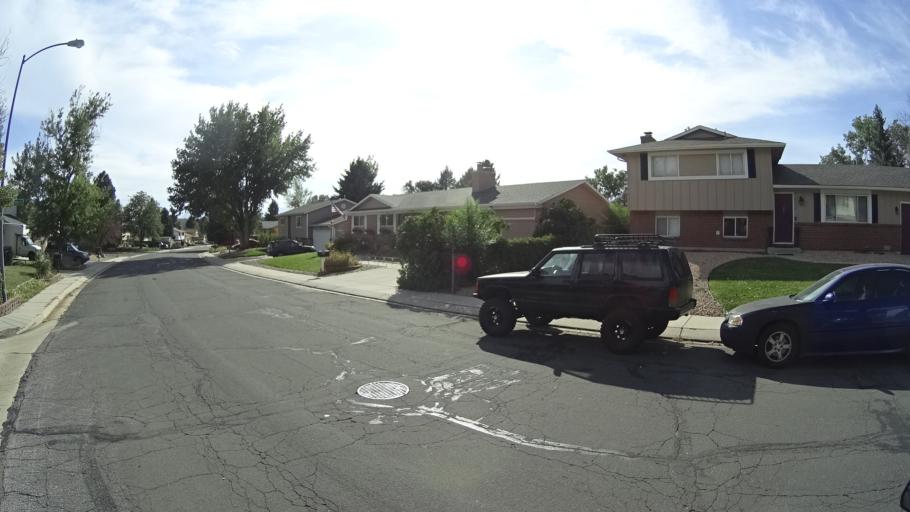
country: US
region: Colorado
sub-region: El Paso County
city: Cimarron Hills
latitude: 38.8982
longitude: -104.7655
